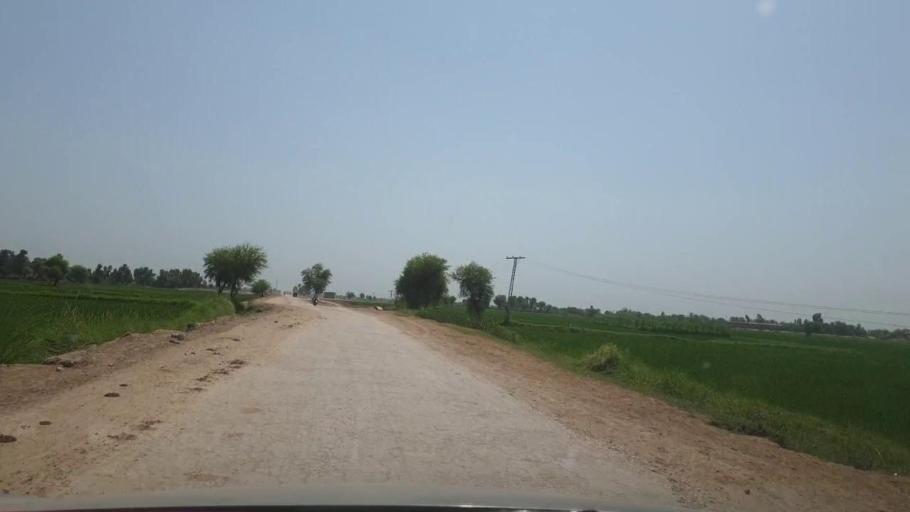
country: PK
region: Sindh
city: Warah
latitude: 27.5042
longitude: 67.7935
